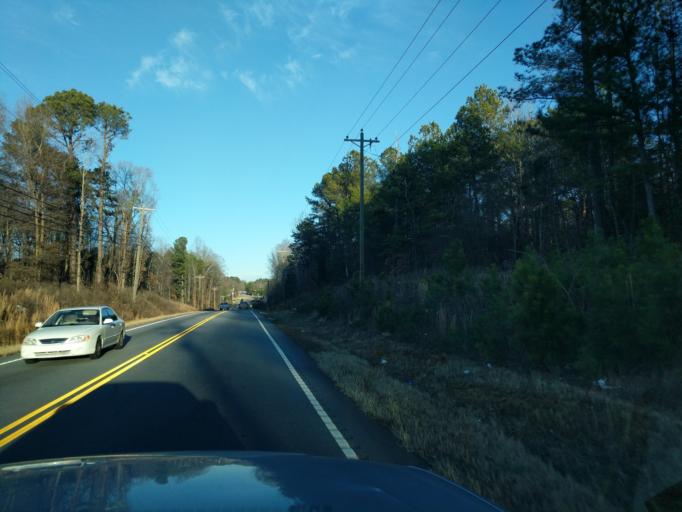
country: US
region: South Carolina
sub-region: Greenville County
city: Fountain Inn
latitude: 34.6710
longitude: -82.2383
